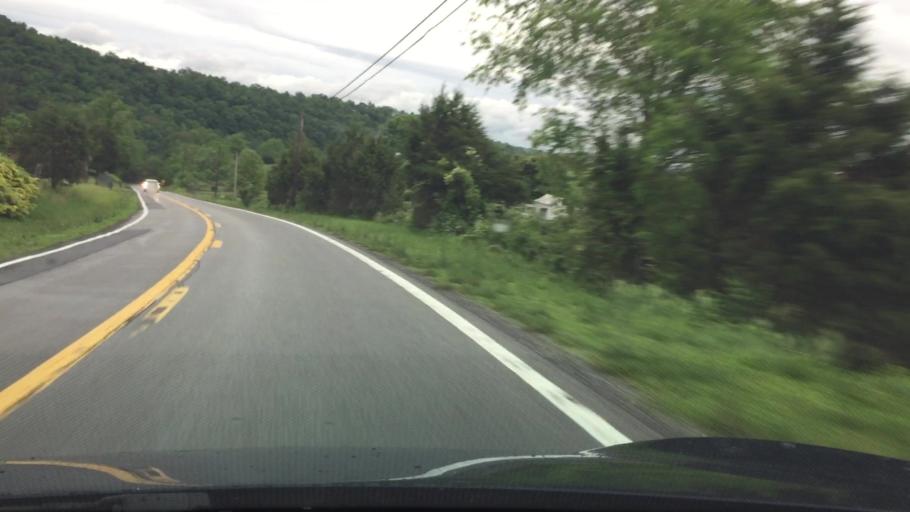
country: US
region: West Virginia
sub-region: Summers County
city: Hinton
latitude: 37.5635
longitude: -80.7939
